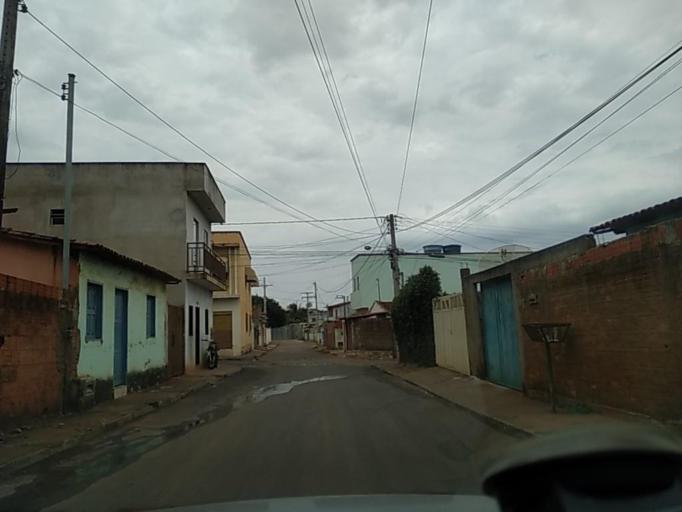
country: BR
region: Bahia
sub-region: Caetite
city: Caetite
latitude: -14.0588
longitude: -42.4804
